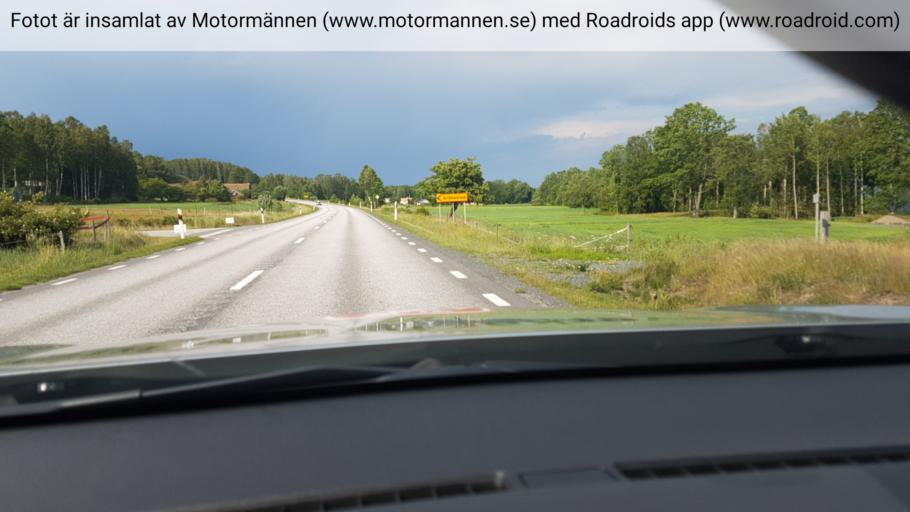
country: SE
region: Joenkoeping
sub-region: Habo Kommun
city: Habo
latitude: 58.0601
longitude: 14.1925
